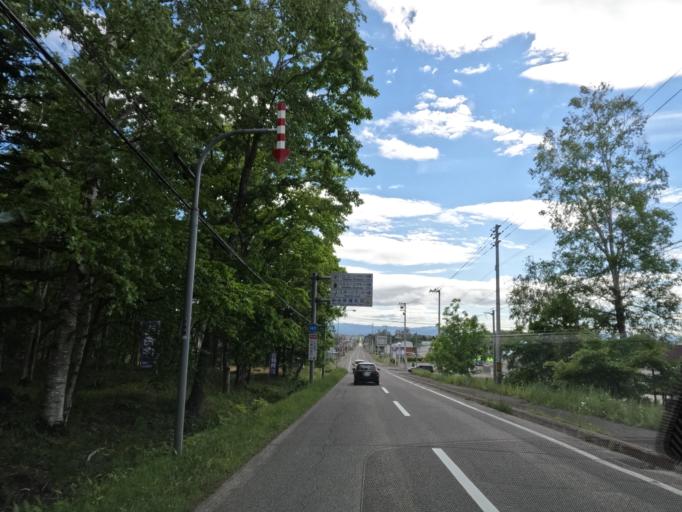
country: JP
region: Hokkaido
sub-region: Asahikawa-shi
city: Asahikawa
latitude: 43.8328
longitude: 142.5330
